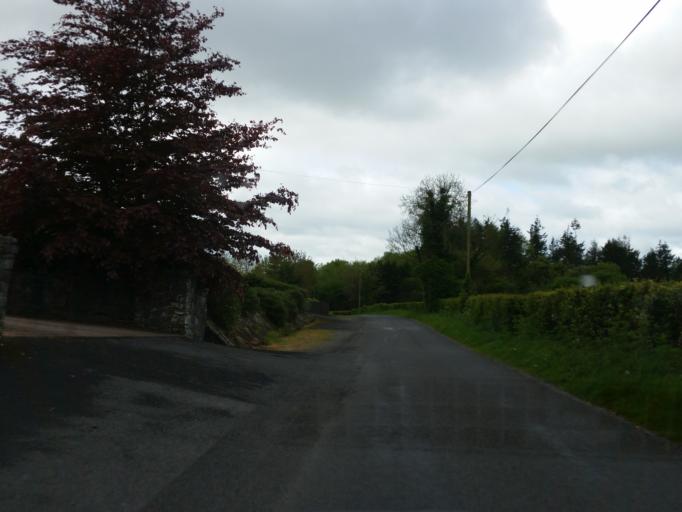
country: GB
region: Northern Ireland
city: Lisnaskea
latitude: 54.3191
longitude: -7.3999
